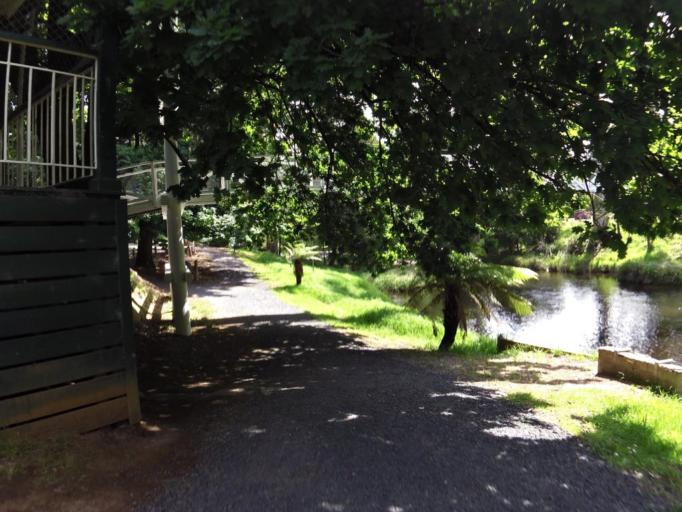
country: AU
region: Victoria
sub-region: Yarra Ranges
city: Millgrove
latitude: -37.7539
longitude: 145.6866
